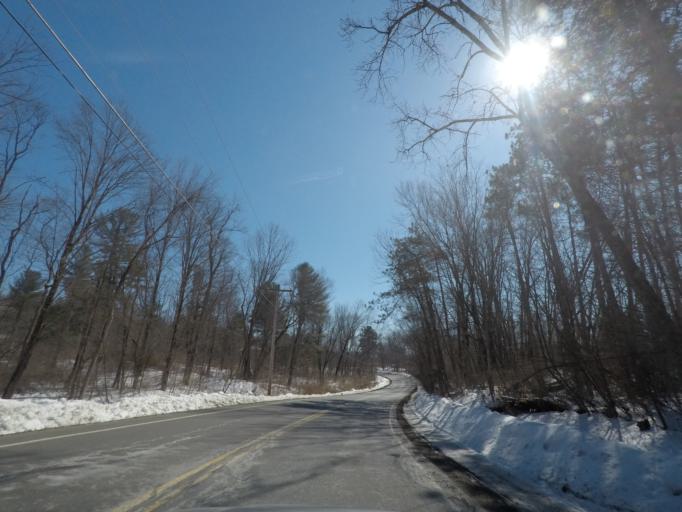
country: US
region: New York
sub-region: Saratoga County
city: Schuylerville
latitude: 43.1234
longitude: -73.5794
